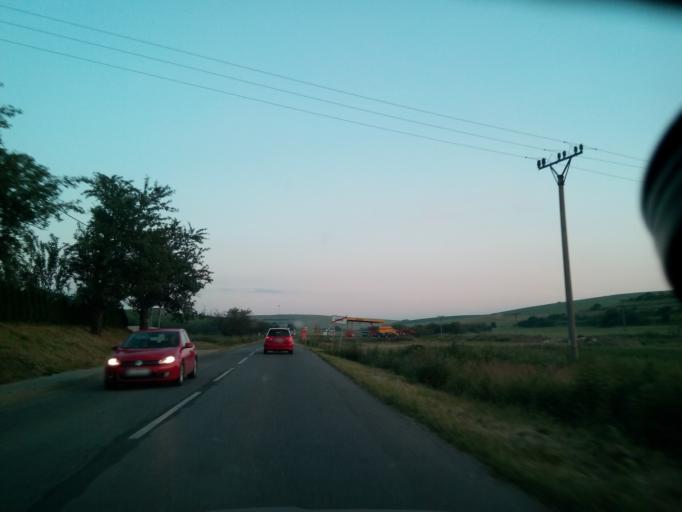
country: SK
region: Presovsky
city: Lubica
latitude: 49.1143
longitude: 20.4444
